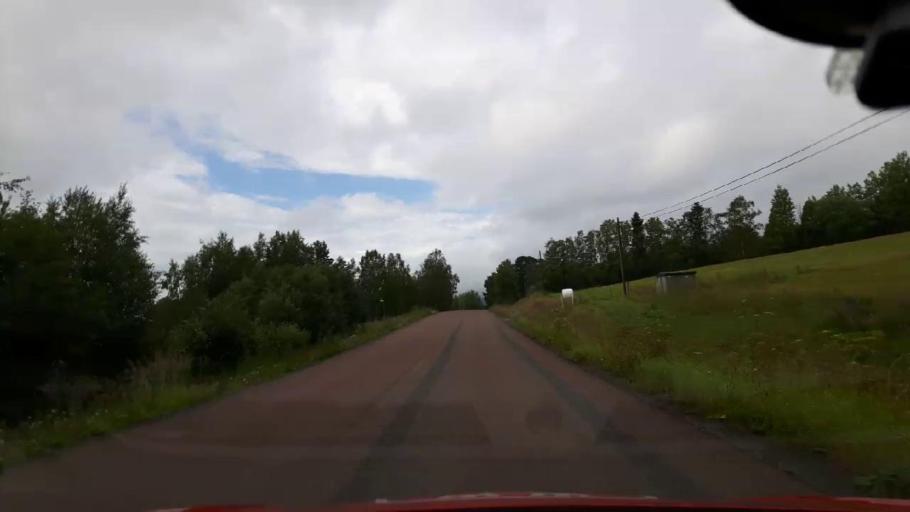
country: SE
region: Jaemtland
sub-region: Krokoms Kommun
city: Valla
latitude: 63.3695
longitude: 14.0413
